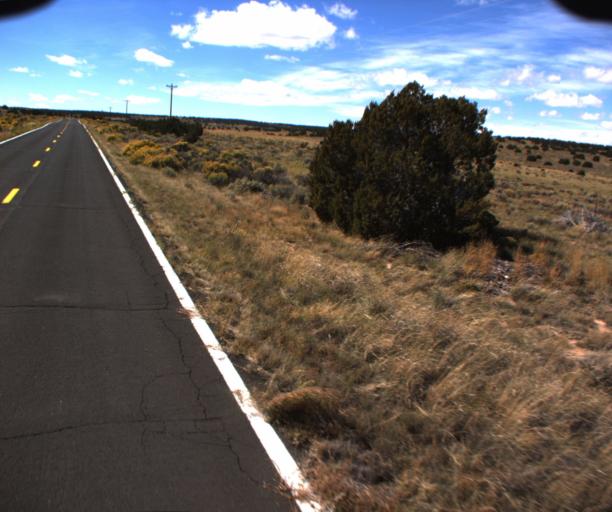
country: US
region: New Mexico
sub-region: McKinley County
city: Zuni Pueblo
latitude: 35.0003
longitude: -109.0888
